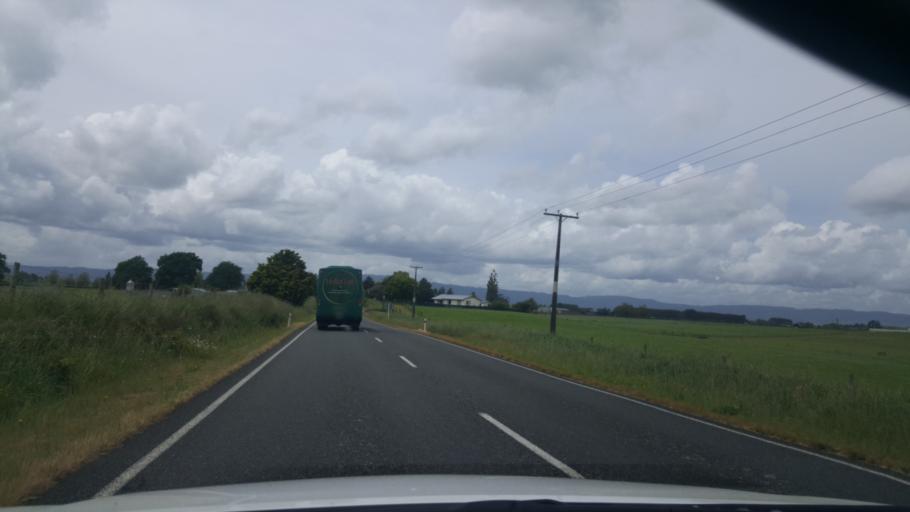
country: NZ
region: Waikato
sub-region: Matamata-Piako District
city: Matamata
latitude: -37.8769
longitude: 175.7182
